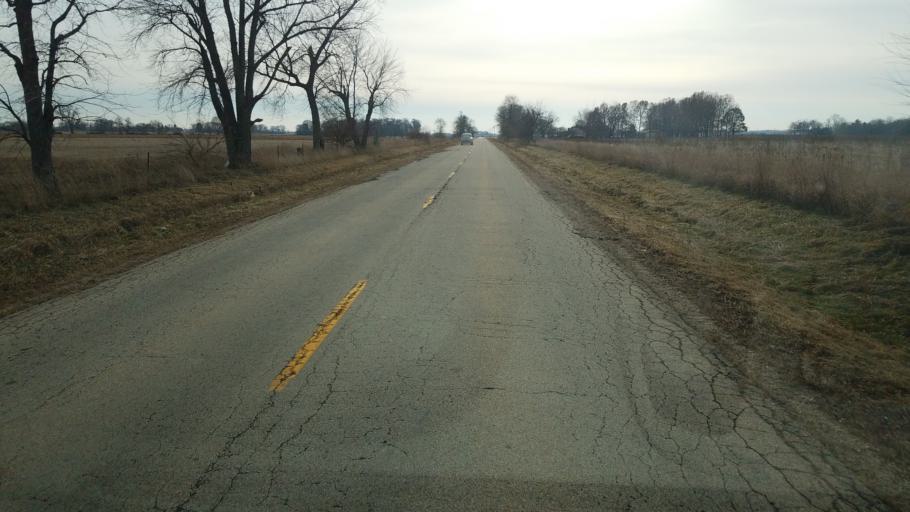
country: US
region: Illinois
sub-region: McHenry County
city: Marengo
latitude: 42.2455
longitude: -88.6524
